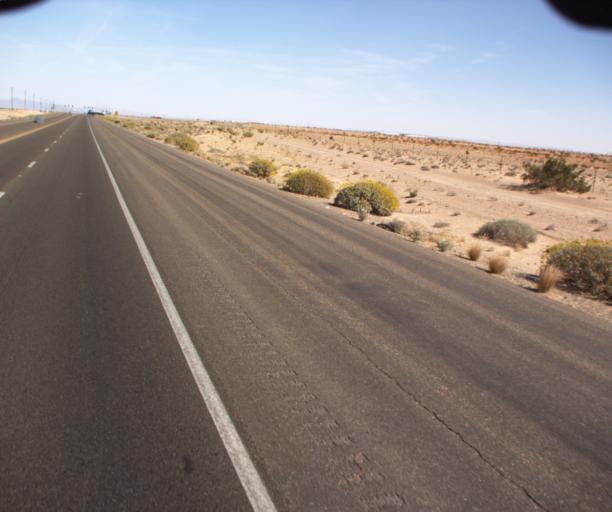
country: MX
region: Sonora
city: San Luis Rio Colorado
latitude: 32.4947
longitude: -114.7067
